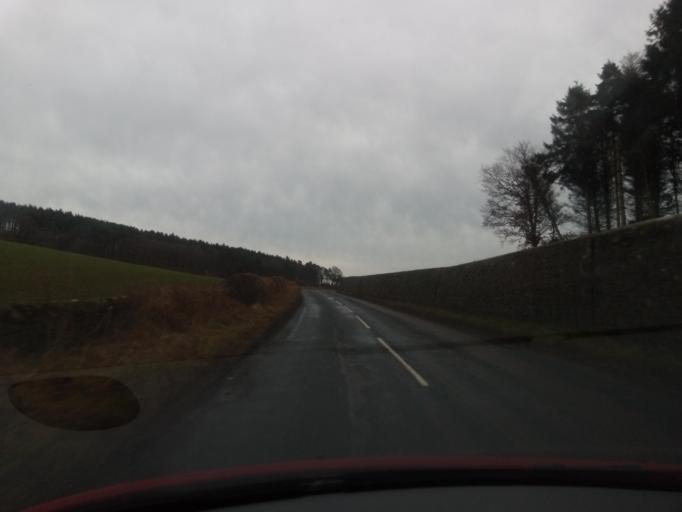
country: GB
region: England
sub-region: Northumberland
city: Alnwick
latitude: 55.4495
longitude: -1.7567
